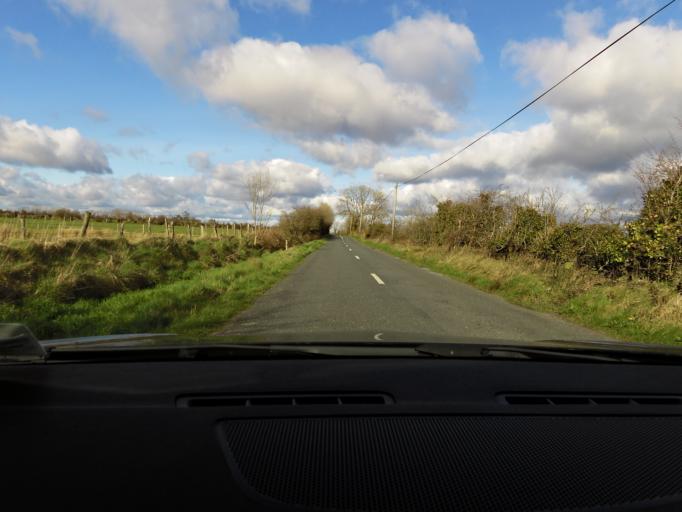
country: IE
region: Connaught
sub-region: County Galway
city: Athenry
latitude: 53.4442
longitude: -8.5611
